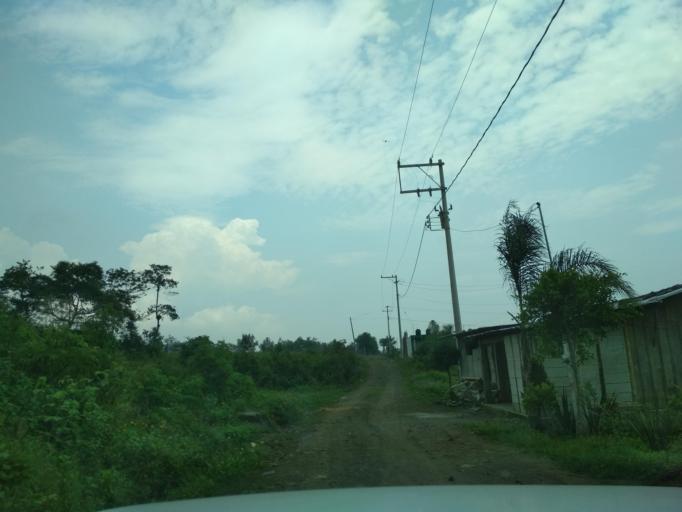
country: MX
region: Veracruz
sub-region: Mariano Escobedo
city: Mariano Escobedo
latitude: 18.9166
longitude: -97.1375
